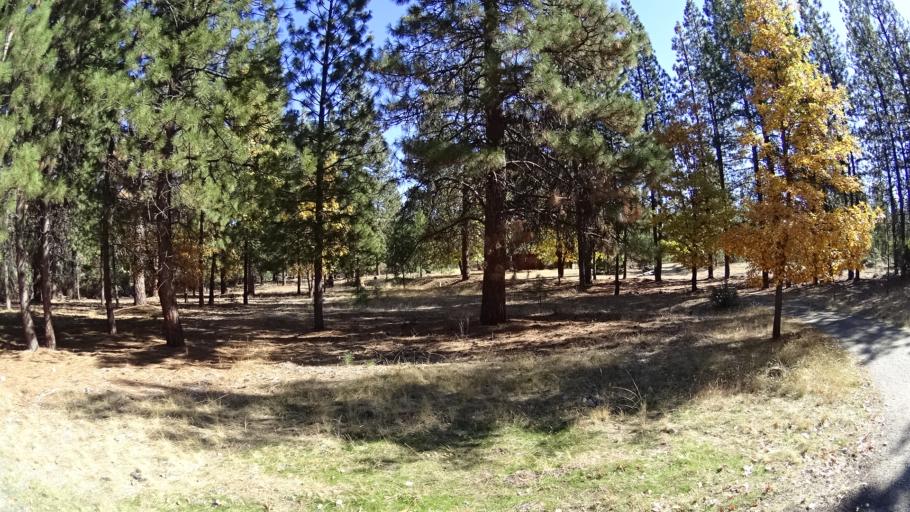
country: US
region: California
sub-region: Siskiyou County
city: Yreka
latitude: 41.5195
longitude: -122.9208
